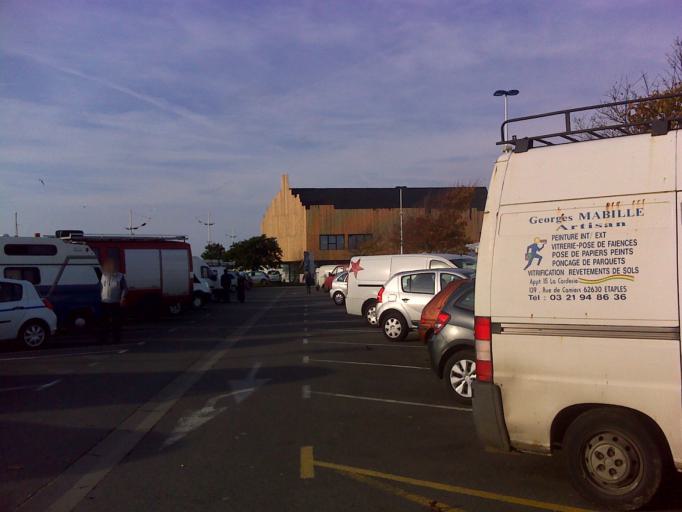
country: FR
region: Nord-Pas-de-Calais
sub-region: Departement du Pas-de-Calais
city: Etaples
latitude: 50.5135
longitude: 1.6355
